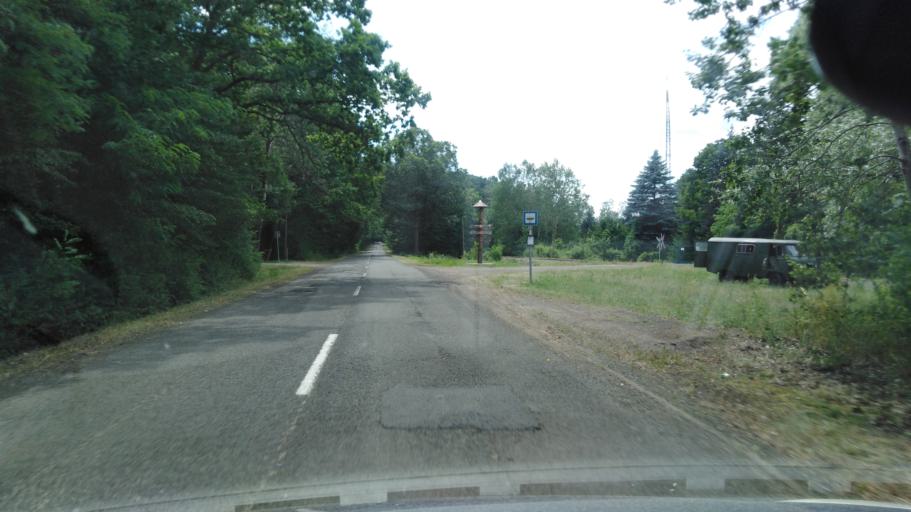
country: HU
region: Nograd
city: Szecseny
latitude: 48.2085
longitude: 19.5564
